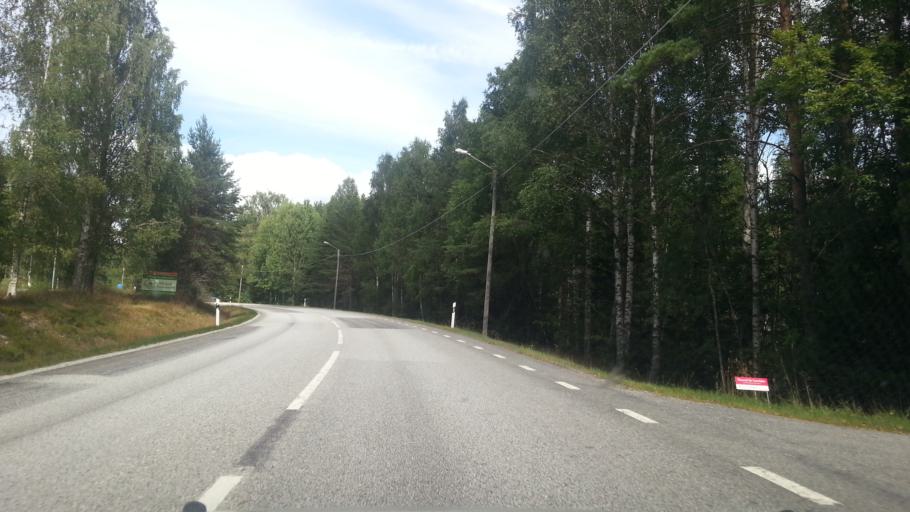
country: SE
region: Vaestmanland
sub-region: Skinnskattebergs Kommun
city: Skinnskatteberg
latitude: 59.8202
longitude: 15.5329
